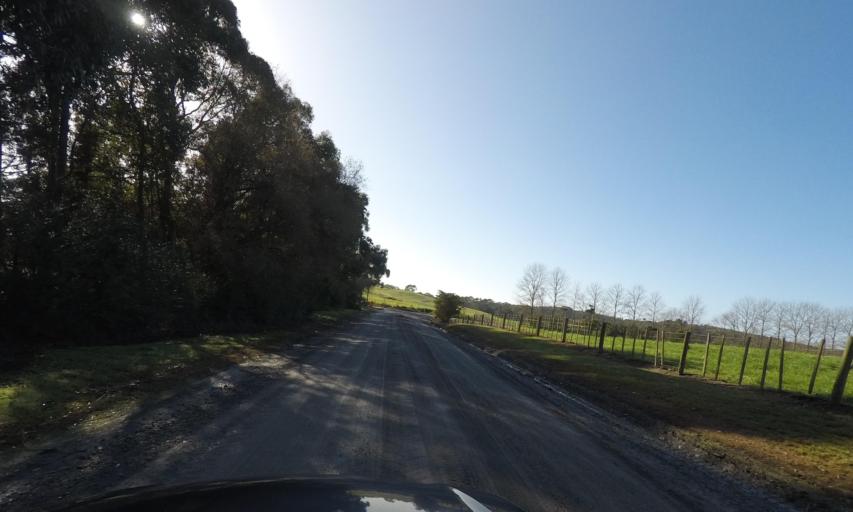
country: NZ
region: Auckland
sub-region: Auckland
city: Wellsford
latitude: -36.1460
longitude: 174.6037
